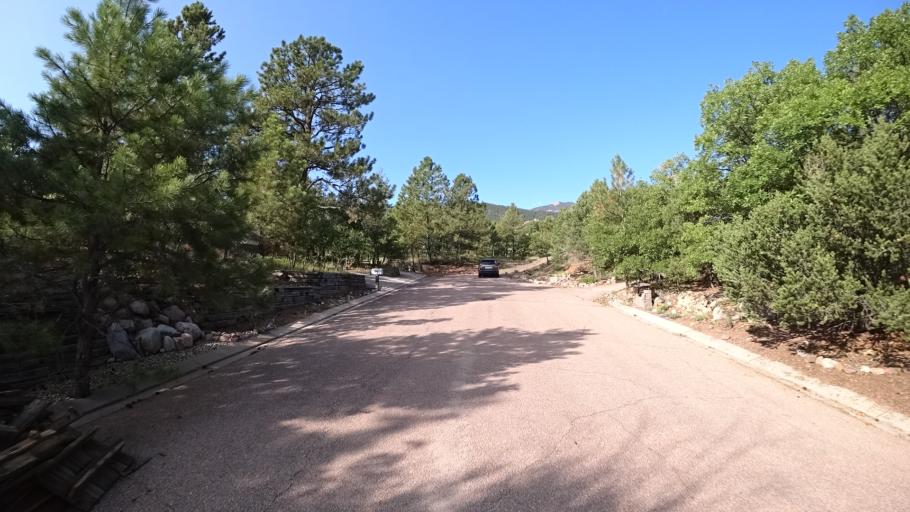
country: US
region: Colorado
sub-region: El Paso County
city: Colorado Springs
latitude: 38.8197
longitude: -104.8727
